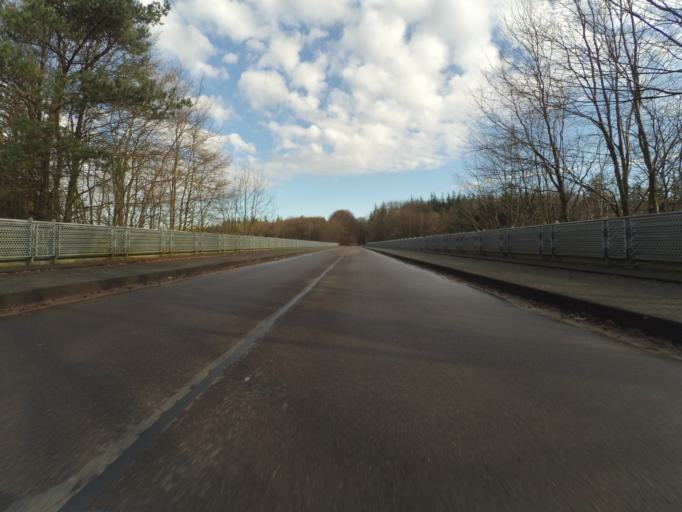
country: NL
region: Gelderland
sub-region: Gemeente Apeldoorn
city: Uddel
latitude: 52.1898
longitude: 5.8442
